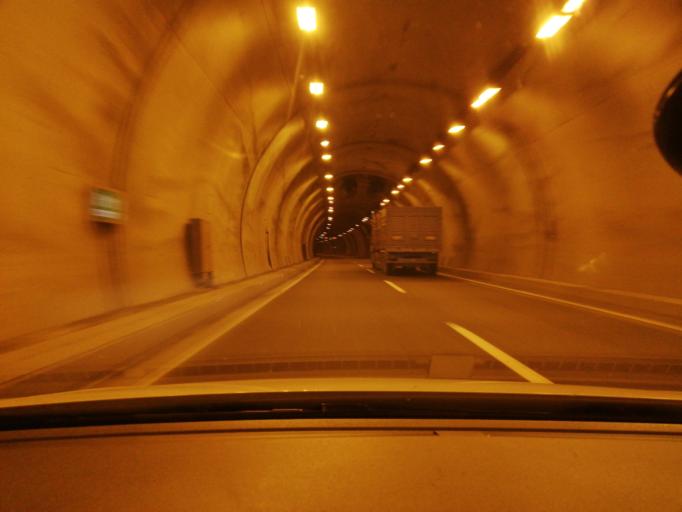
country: TR
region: Zonguldak
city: Alapli
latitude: 41.1546
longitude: 31.3548
